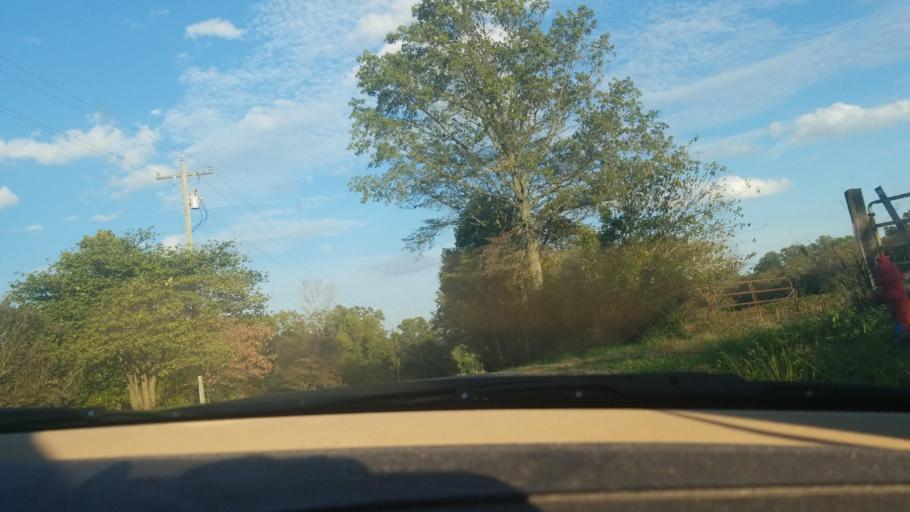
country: US
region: Illinois
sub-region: Saline County
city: Carrier Mills
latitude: 37.7719
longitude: -88.7274
